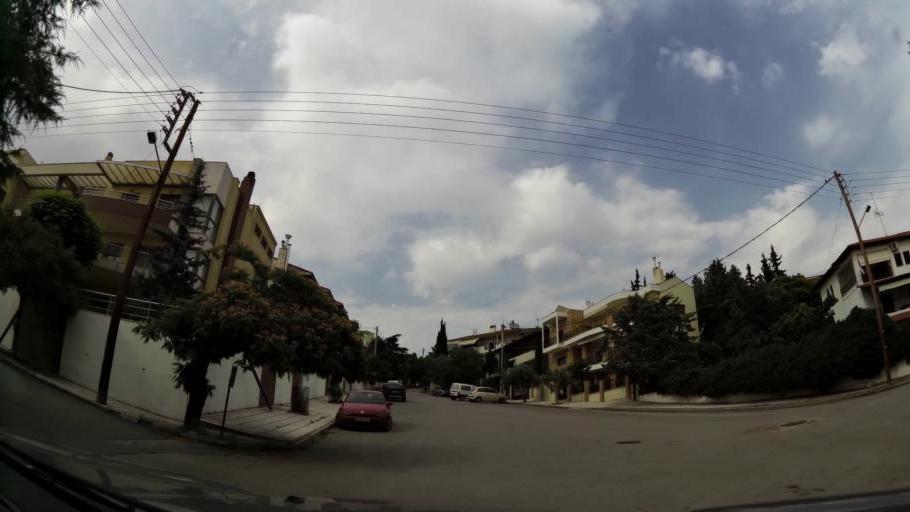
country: GR
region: Central Macedonia
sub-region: Nomos Thessalonikis
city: Oraiokastro
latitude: 40.7137
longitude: 22.9247
